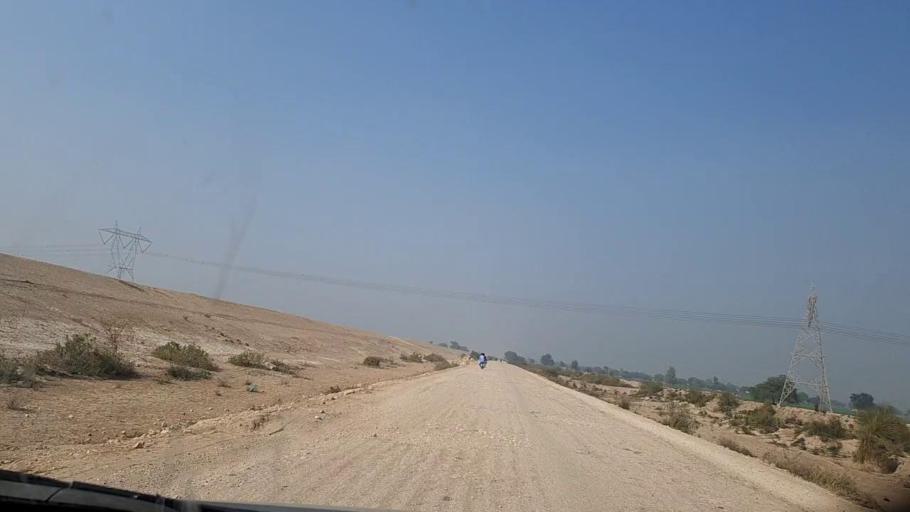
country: PK
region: Sindh
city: Moro
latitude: 26.7099
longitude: 67.9251
